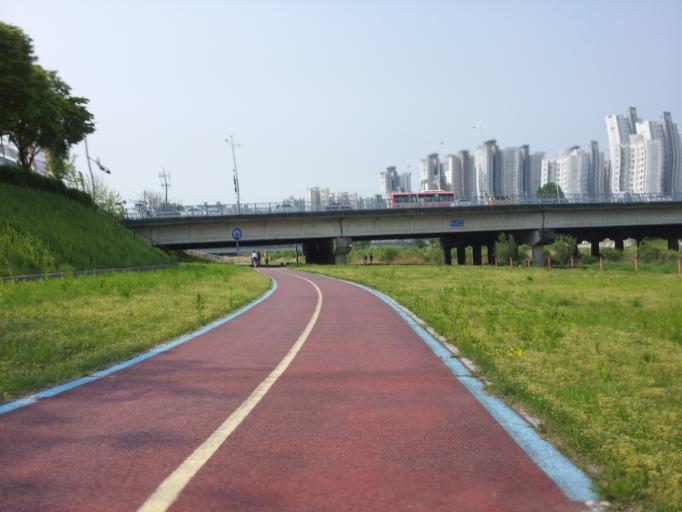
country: KR
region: Daejeon
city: Daejeon
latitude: 36.3522
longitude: 127.3510
